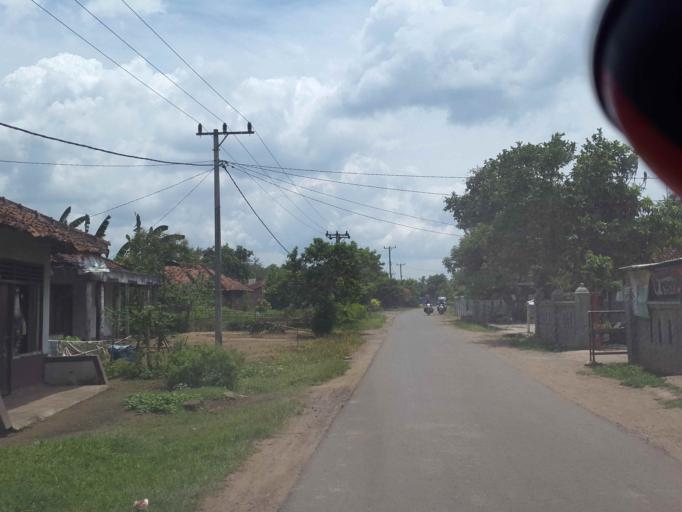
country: ID
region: Lampung
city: Natar
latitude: -5.3125
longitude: 105.2199
